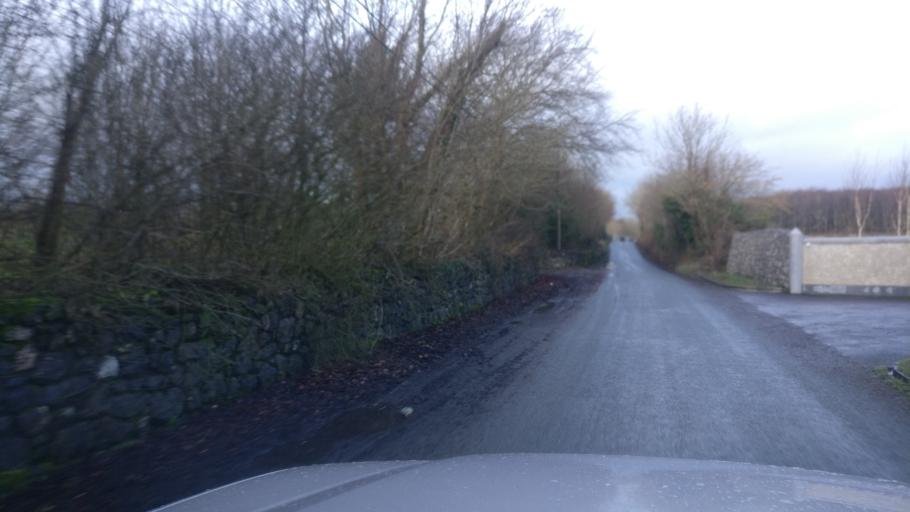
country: IE
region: Connaught
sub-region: County Galway
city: Athenry
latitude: 53.2521
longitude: -8.7213
